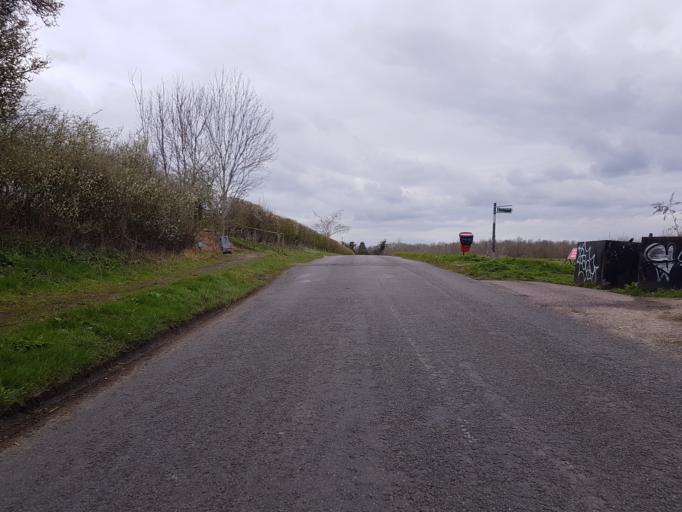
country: GB
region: England
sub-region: Cambridgeshire
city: Girton
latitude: 52.2196
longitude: 0.0521
